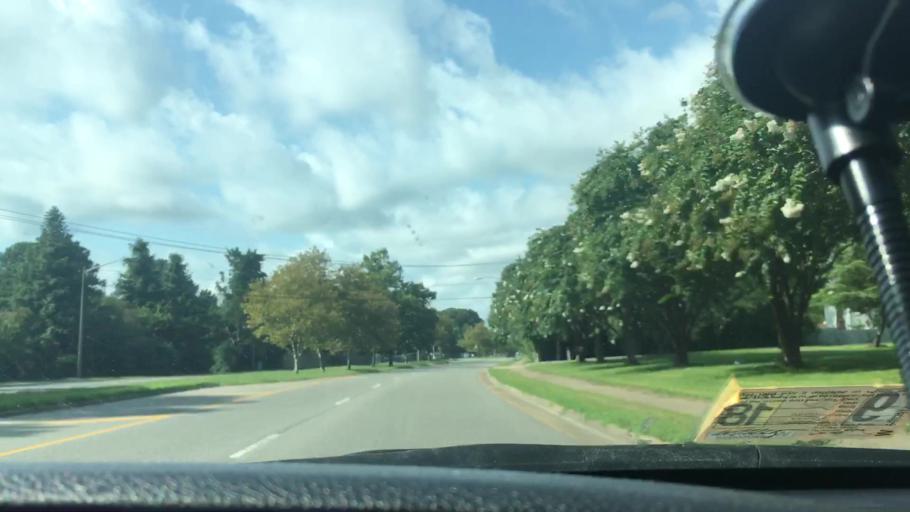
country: US
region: Virginia
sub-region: City of Virginia Beach
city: Virginia Beach
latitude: 36.8719
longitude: -76.0403
